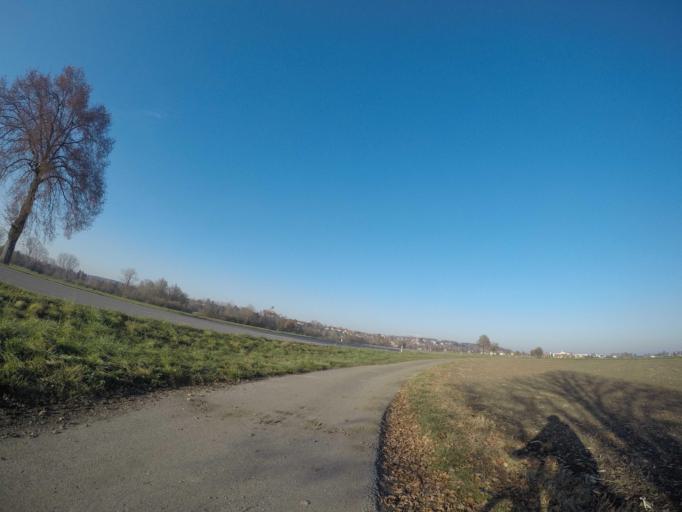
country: DE
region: Baden-Wuerttemberg
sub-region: Tuebingen Region
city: Rottenacker
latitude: 48.2241
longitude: 9.6860
